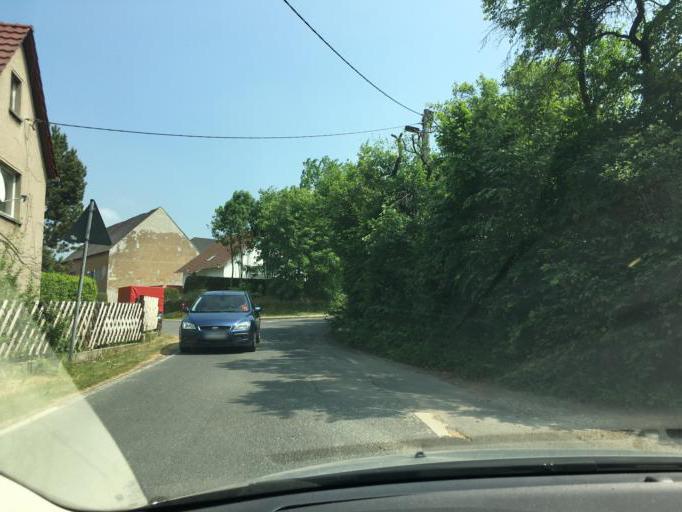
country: DE
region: Saxony
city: Bad Lausick
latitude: 51.1839
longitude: 12.6607
